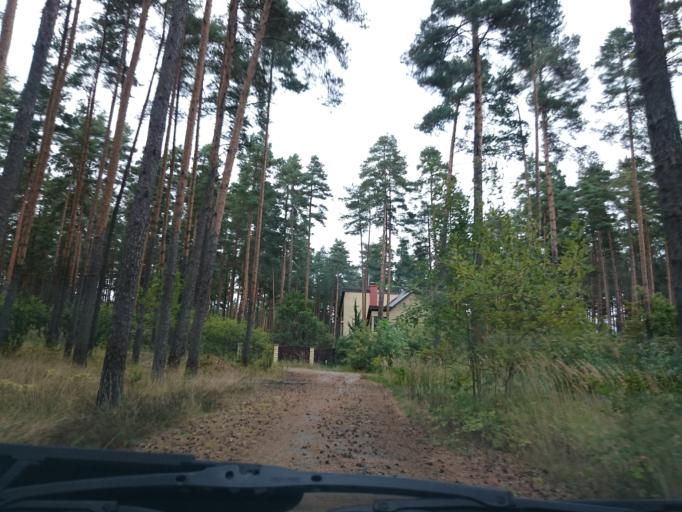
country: LV
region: Adazi
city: Adazi
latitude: 57.0538
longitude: 24.3234
